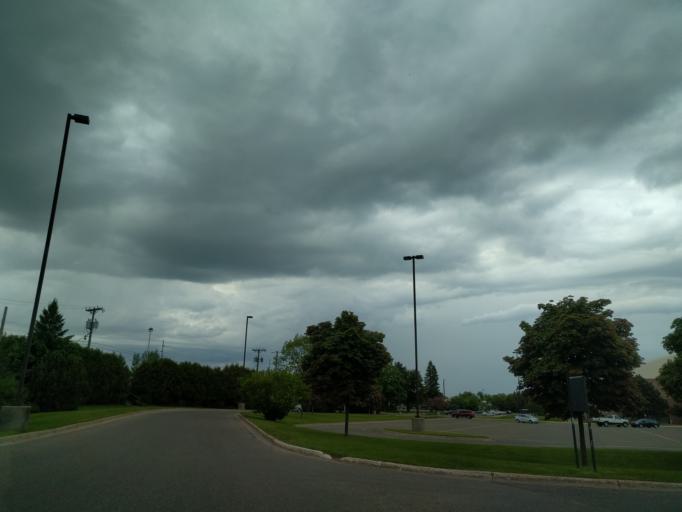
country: US
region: Michigan
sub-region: Marquette County
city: Marquette
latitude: 46.5569
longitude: -87.3948
